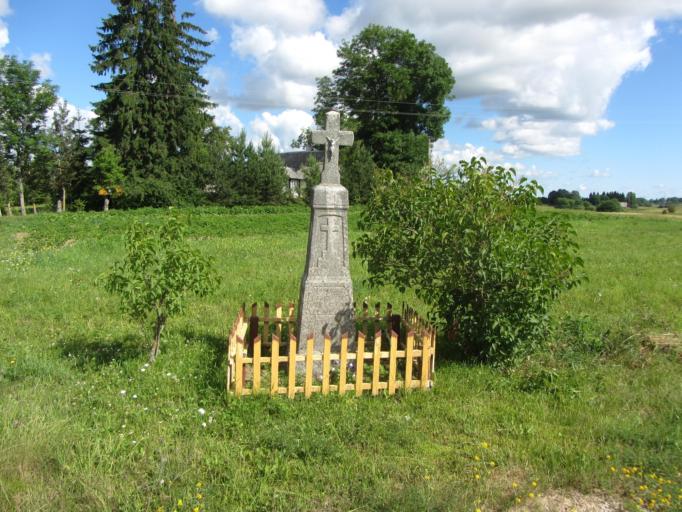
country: LT
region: Utenos apskritis
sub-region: Utena
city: Utena
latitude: 55.5027
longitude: 25.6858
